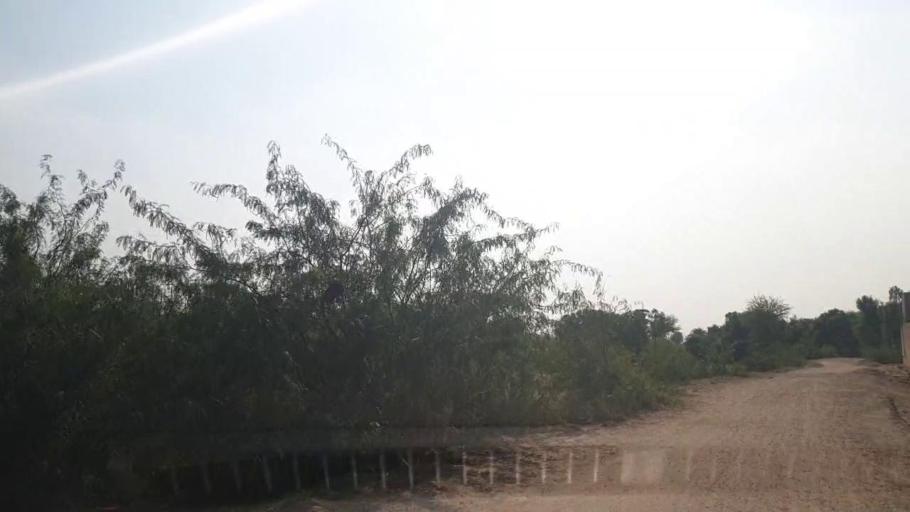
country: PK
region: Sindh
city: Hyderabad
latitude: 25.4683
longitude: 68.3790
